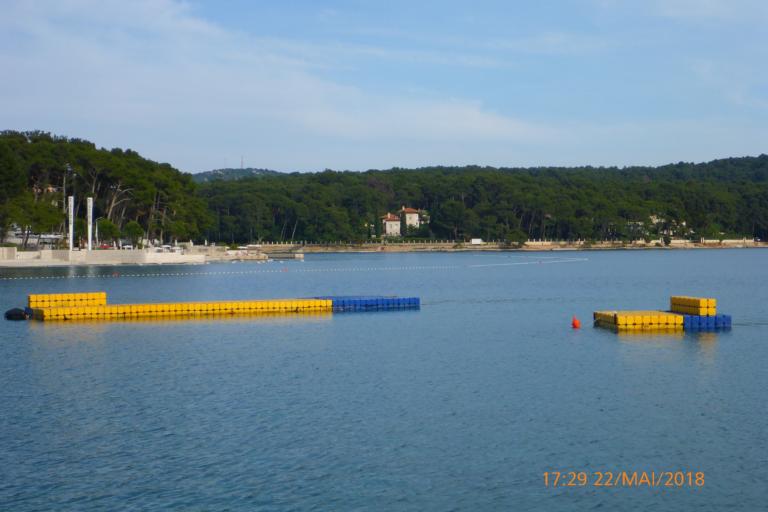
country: HR
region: Primorsko-Goranska
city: Mali Losinj
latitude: 44.5319
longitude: 14.4511
